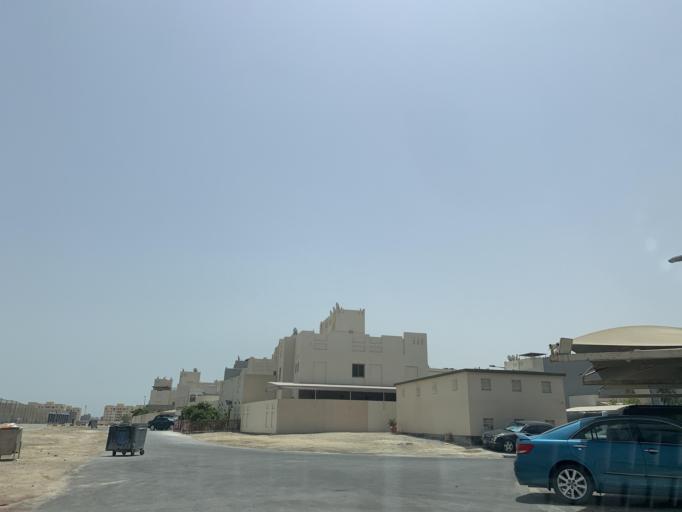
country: BH
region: Northern
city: Sitrah
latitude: 26.1479
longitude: 50.5911
